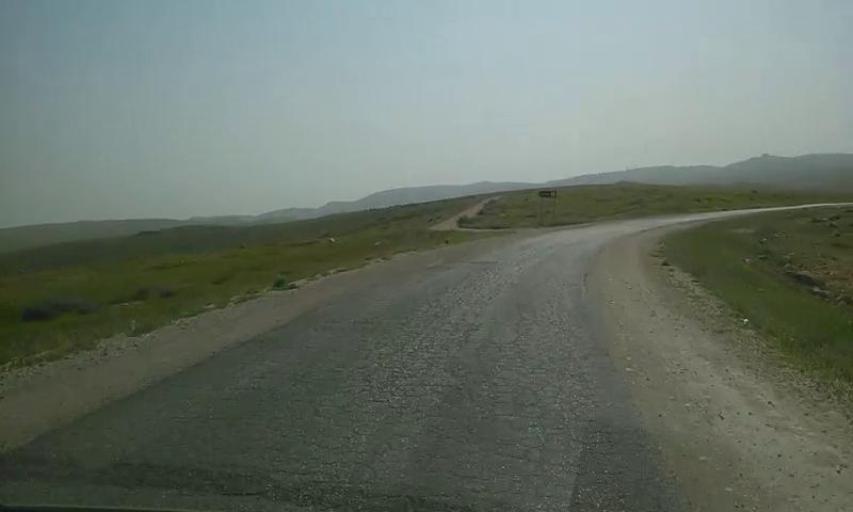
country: PS
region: West Bank
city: An Nuway`imah
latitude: 31.9205
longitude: 35.4185
